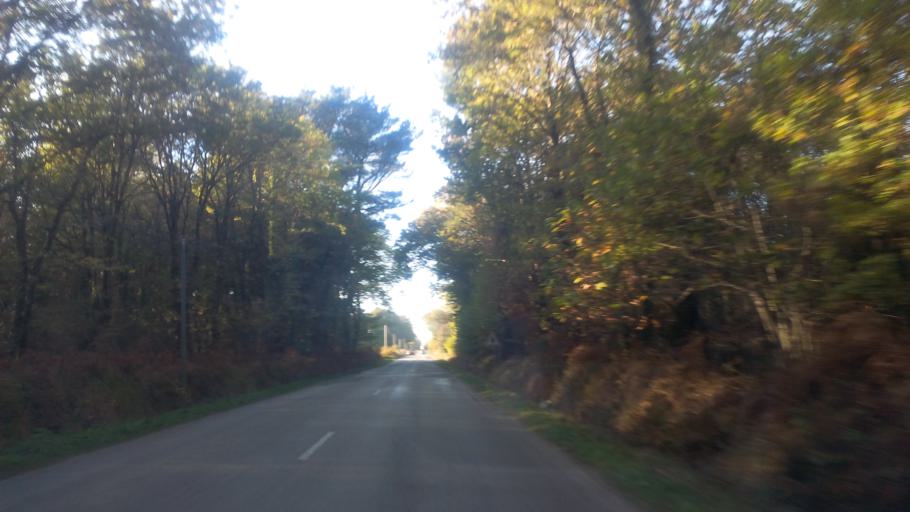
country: FR
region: Brittany
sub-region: Departement du Morbihan
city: Elven
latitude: 47.7128
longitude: -2.5676
